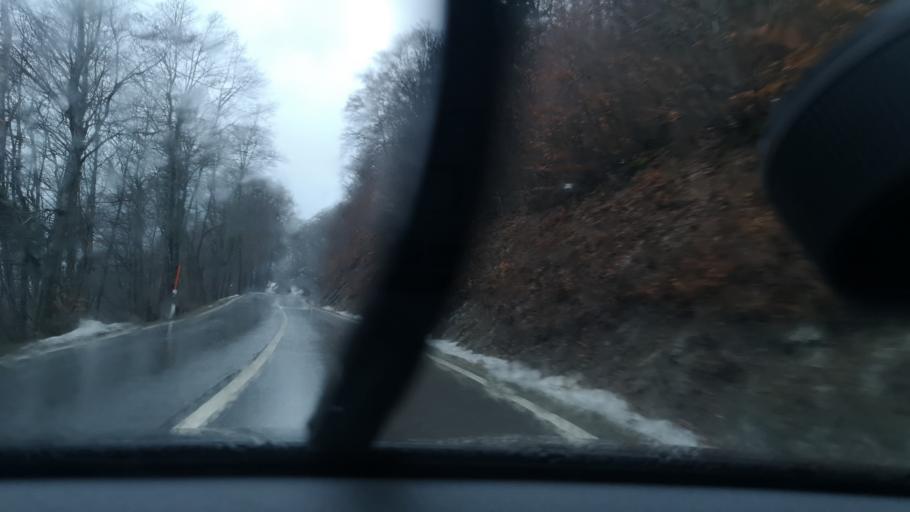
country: CH
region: Neuchatel
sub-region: Le Locle District
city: Les Ponts-de-Martel
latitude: 46.9584
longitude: 6.7535
